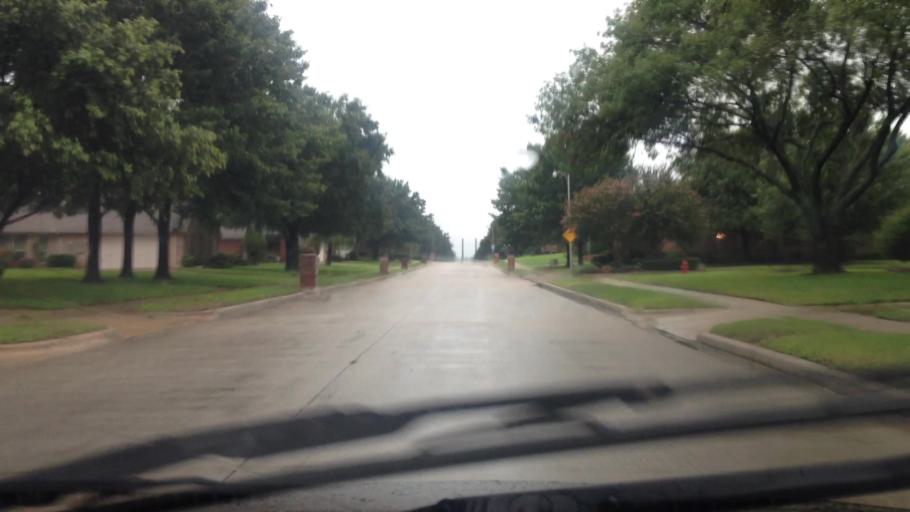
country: US
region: Texas
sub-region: Tarrant County
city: Colleyville
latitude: 32.8996
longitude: -97.1952
